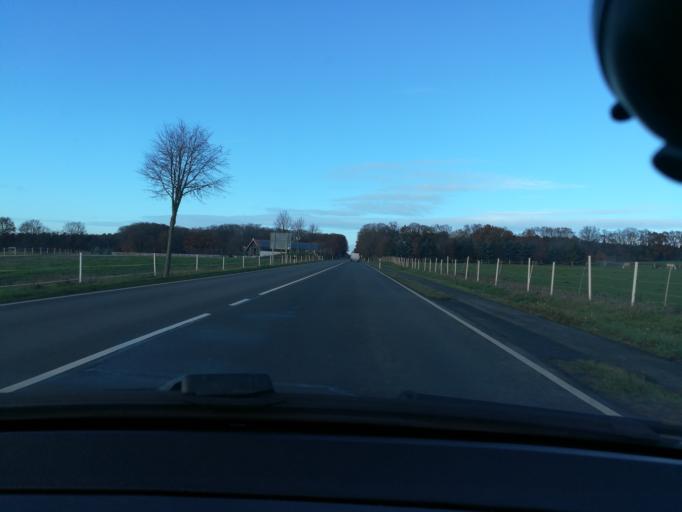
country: DE
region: Lower Saxony
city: Kirchdorf
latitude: 52.5663
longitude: 8.8514
